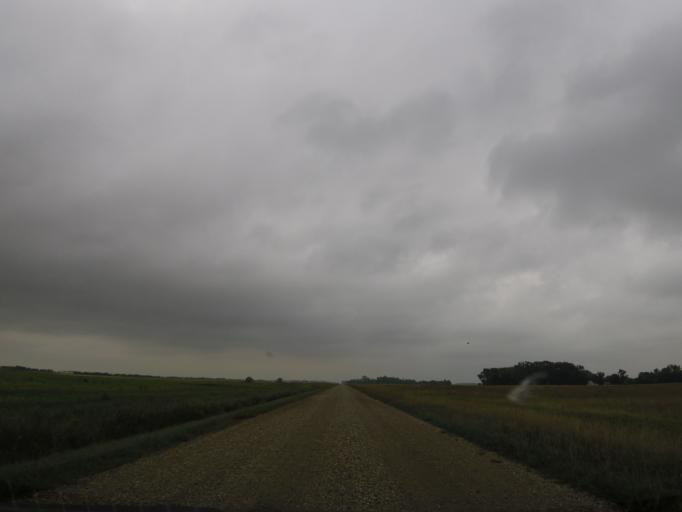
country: US
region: North Dakota
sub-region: Walsh County
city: Grafton
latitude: 48.4726
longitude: -97.1686
